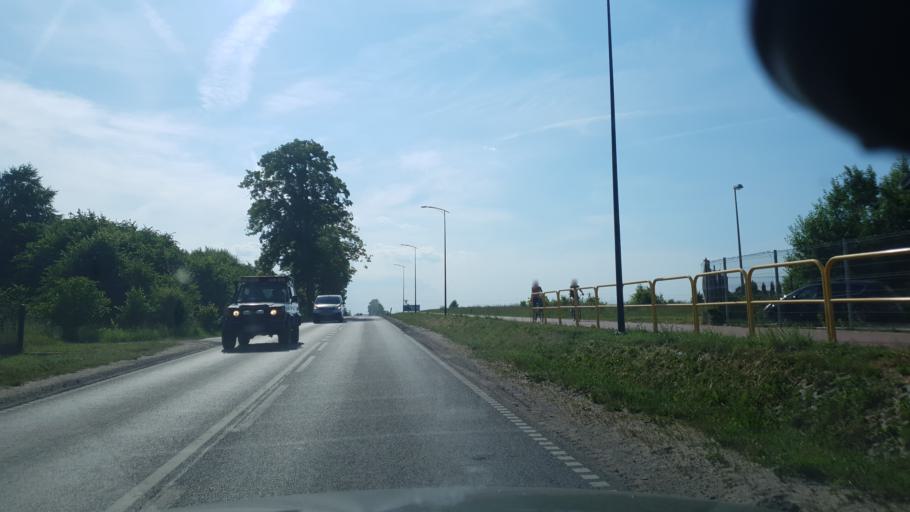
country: PL
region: Pomeranian Voivodeship
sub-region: Powiat kartuski
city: Chwaszczyno
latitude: 54.4427
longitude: 18.4384
